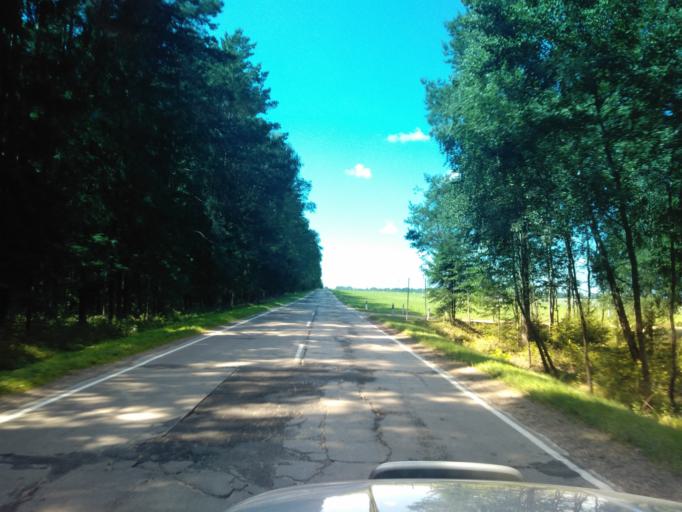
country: BY
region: Minsk
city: Stan'kava
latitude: 53.6231
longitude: 27.2928
